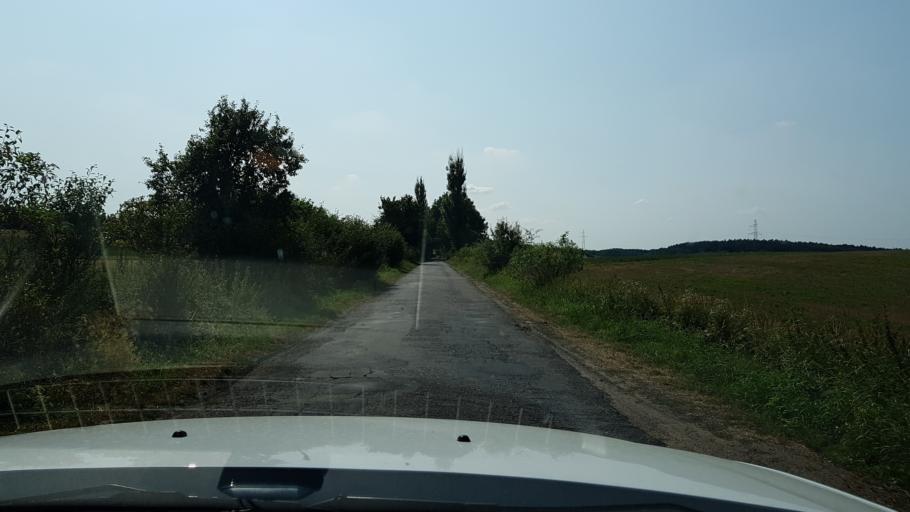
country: PL
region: West Pomeranian Voivodeship
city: Trzcinsko Zdroj
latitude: 52.9275
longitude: 14.5301
